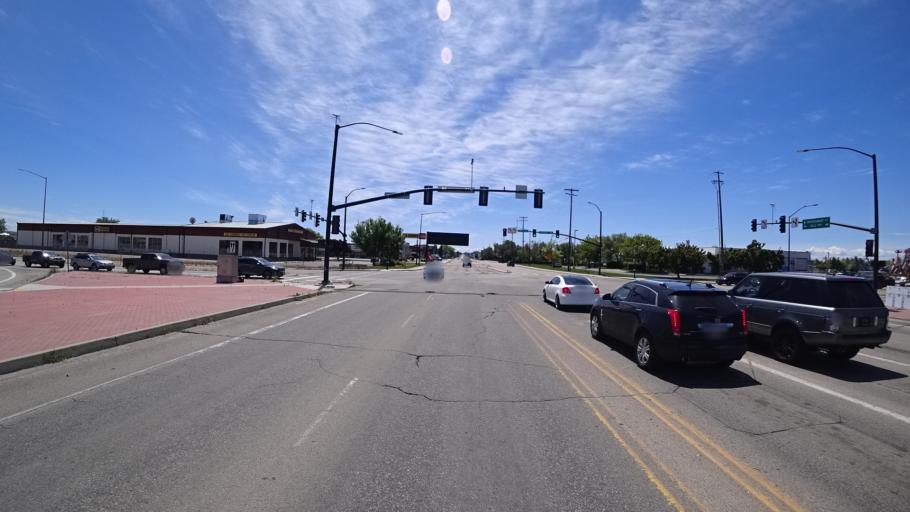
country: US
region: Idaho
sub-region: Ada County
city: Garden City
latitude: 43.5879
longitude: -116.2741
